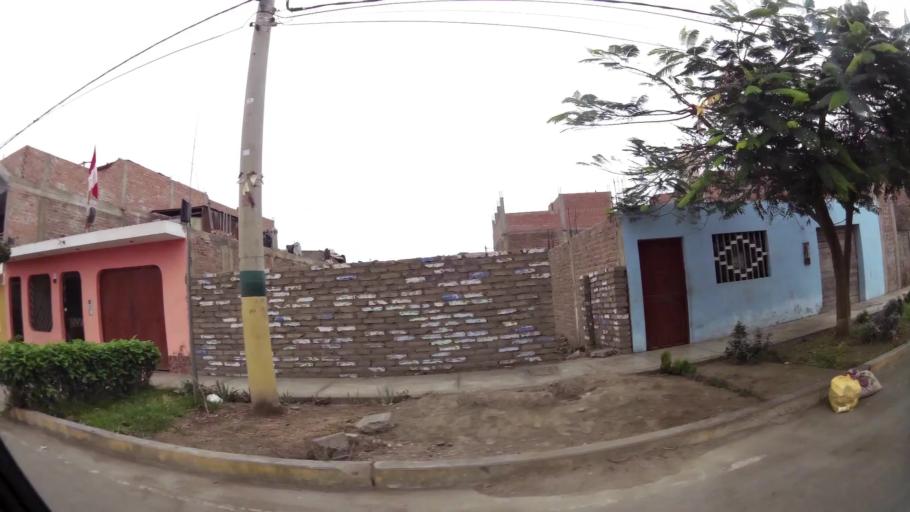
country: PE
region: Lima
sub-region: Barranca
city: Barranca
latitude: -10.7616
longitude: -77.7592
